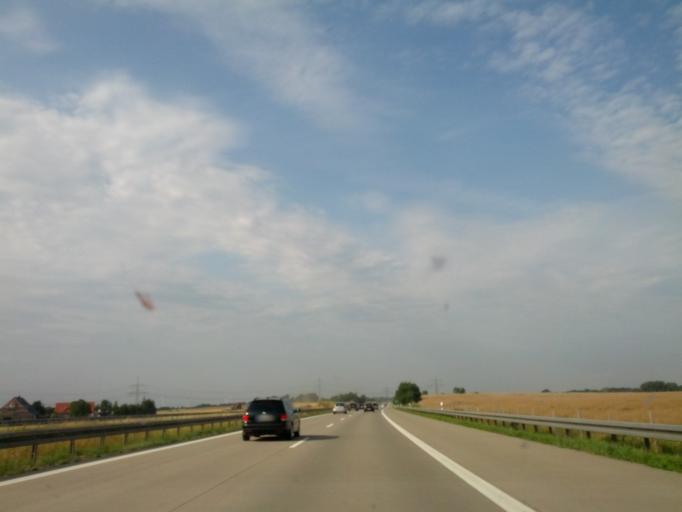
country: DE
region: Mecklenburg-Vorpommern
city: Kavelstorf
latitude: 53.9854
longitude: 12.1966
